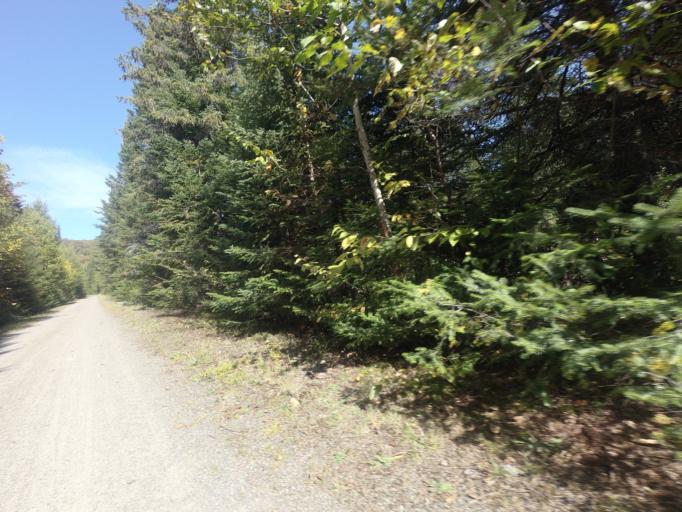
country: CA
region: Quebec
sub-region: Laurentides
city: Sainte-Agathe-des-Monts
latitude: 46.1014
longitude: -74.3637
